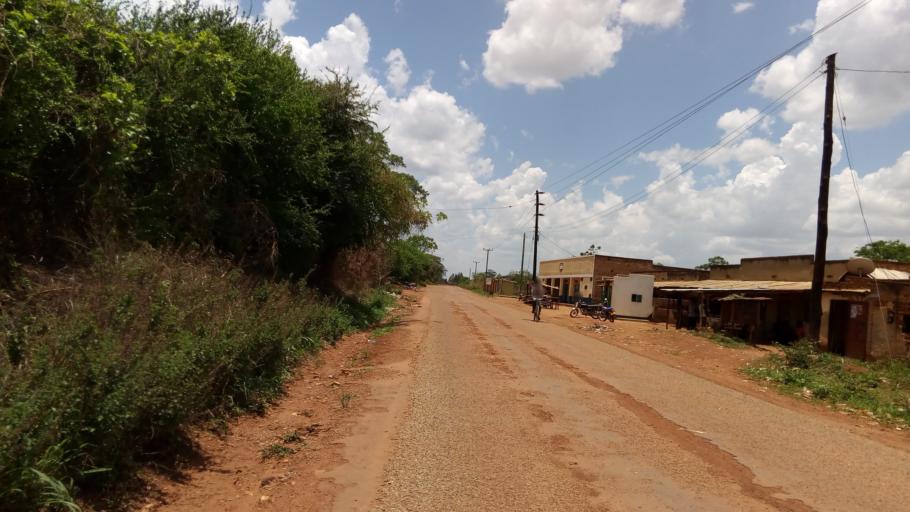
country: UG
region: Northern Region
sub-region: Gulu District
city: Gulu
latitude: 2.7876
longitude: 32.3458
